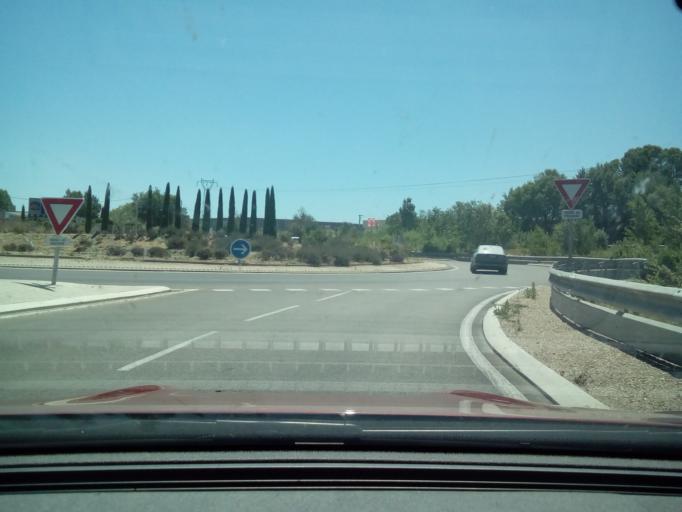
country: FR
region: Provence-Alpes-Cote d'Azur
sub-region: Departement des Bouches-du-Rhone
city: Rousset
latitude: 43.4704
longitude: 5.5953
